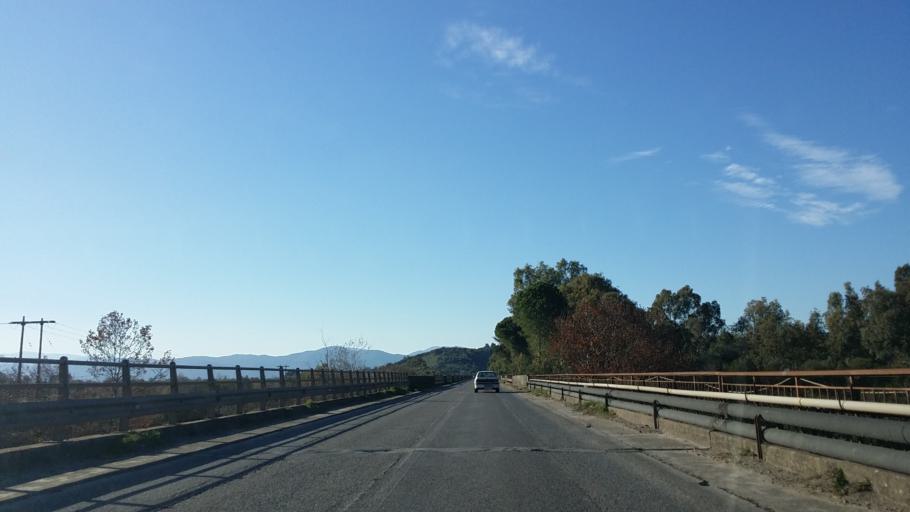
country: GR
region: West Greece
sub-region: Nomos Aitolias kai Akarnanias
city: Neapolis
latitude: 38.6700
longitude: 21.3370
